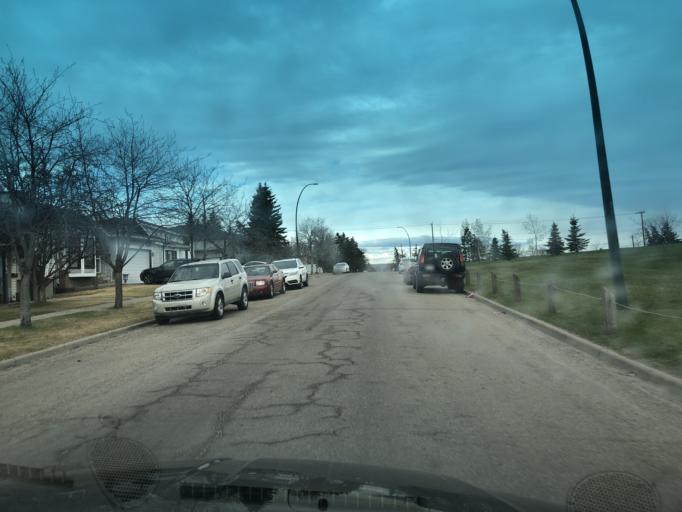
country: CA
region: Alberta
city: Calgary
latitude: 51.0743
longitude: -114.0115
